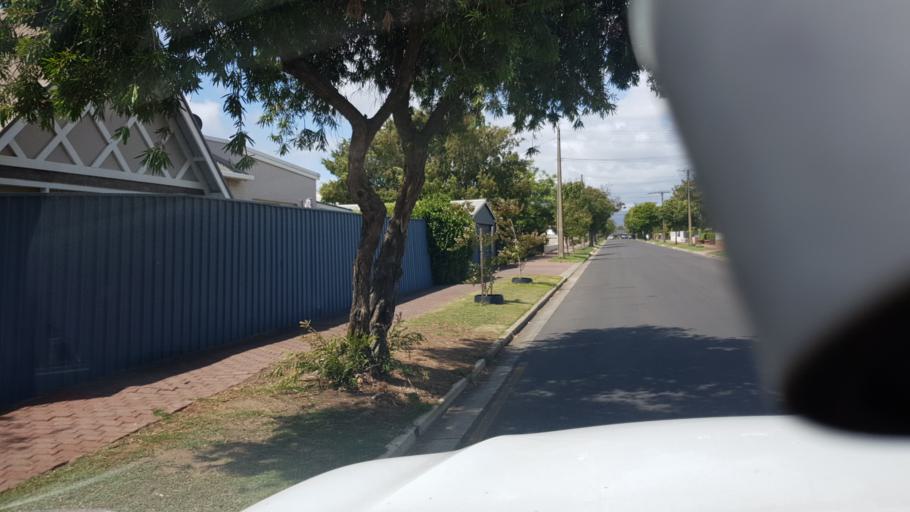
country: AU
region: South Australia
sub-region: Holdfast Bay
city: Glenelg East
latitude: -34.9846
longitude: 138.5244
